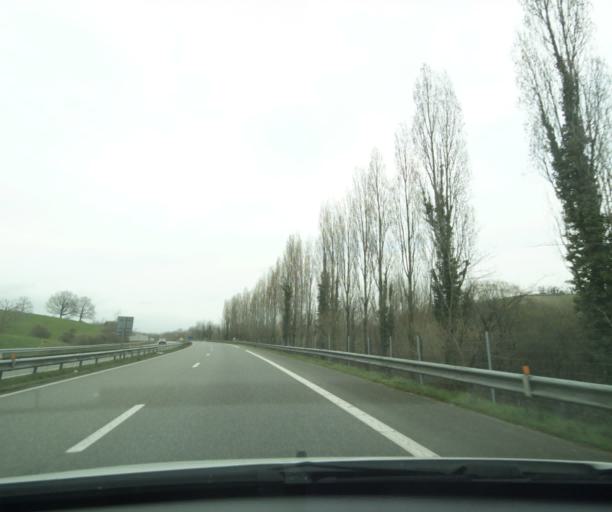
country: FR
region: Aquitaine
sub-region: Departement des Pyrenees-Atlantiques
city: Urt
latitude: 43.4578
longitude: -1.2931
